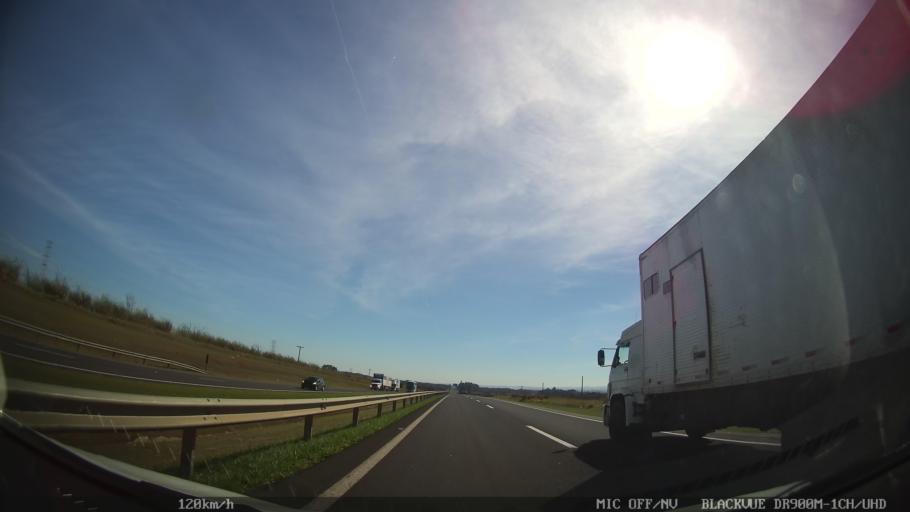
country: BR
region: Sao Paulo
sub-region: Pirassununga
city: Pirassununga
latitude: -21.9774
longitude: -47.4528
